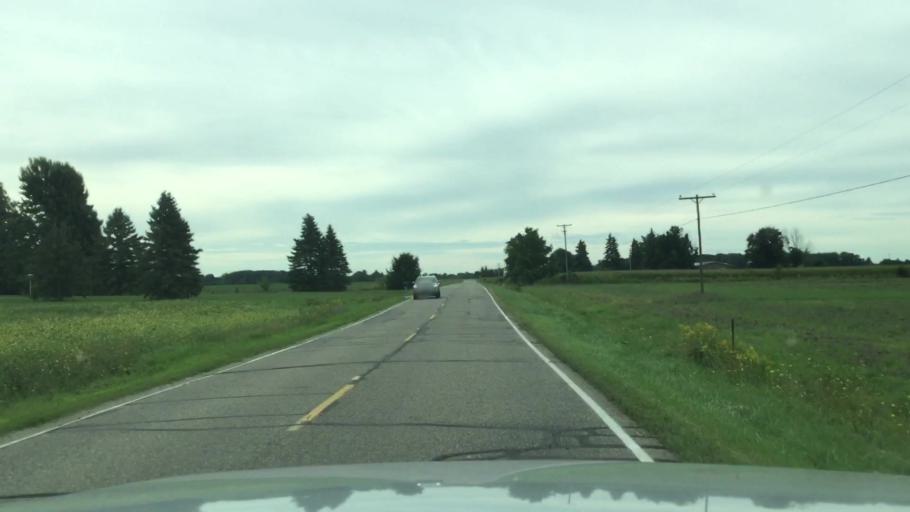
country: US
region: Michigan
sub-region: Genesee County
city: Montrose
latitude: 43.0781
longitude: -83.9877
